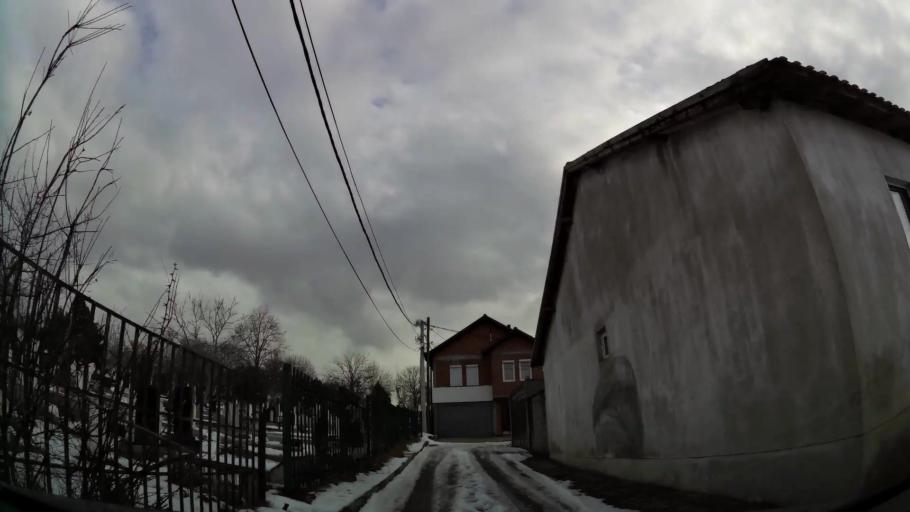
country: XK
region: Pristina
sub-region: Komuna e Prishtines
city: Pristina
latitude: 42.6716
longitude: 21.1516
